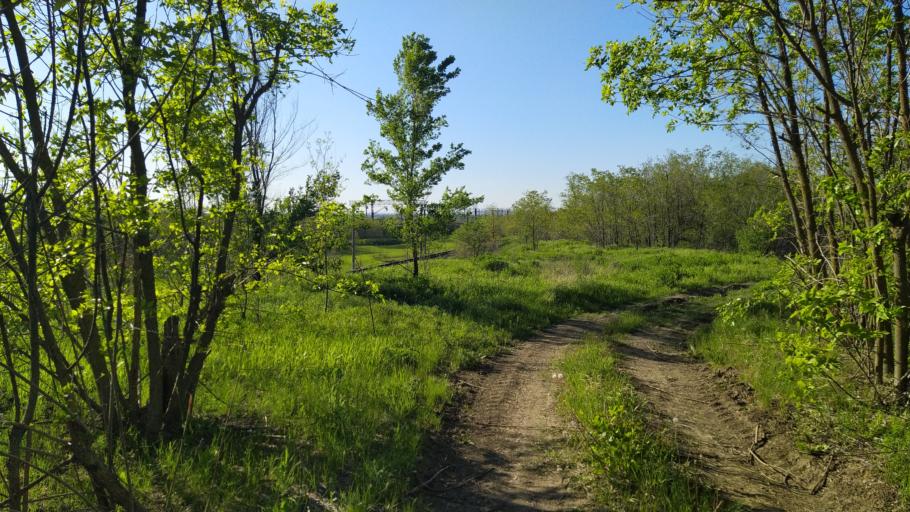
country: RU
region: Rostov
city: Bataysk
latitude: 47.0754
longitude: 39.7168
